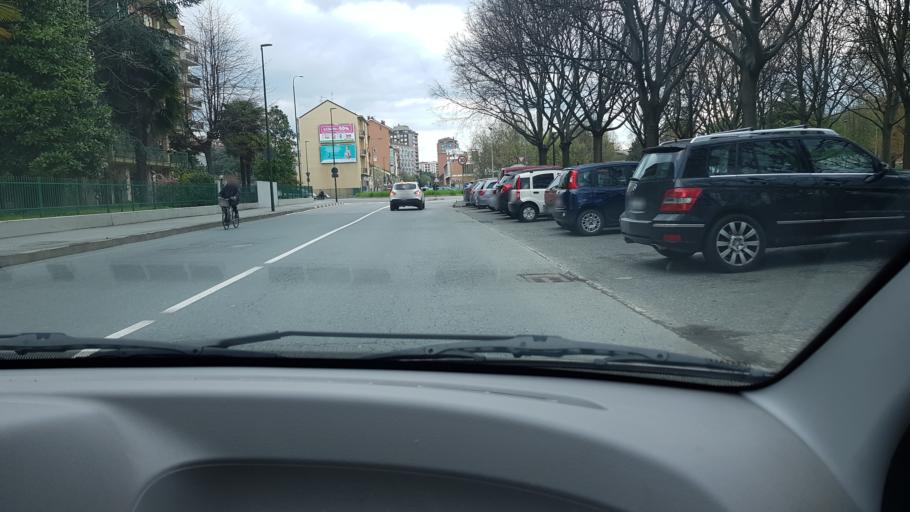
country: IT
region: Piedmont
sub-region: Provincia di Torino
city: Nichelino
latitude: 45.0170
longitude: 7.6386
